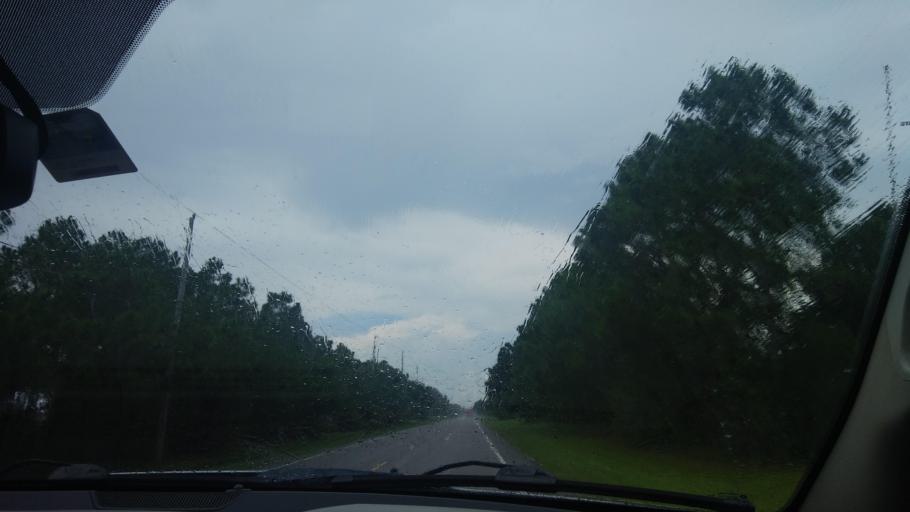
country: US
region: Florida
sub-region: Indian River County
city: Fellsmere
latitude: 27.8135
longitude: -80.6074
